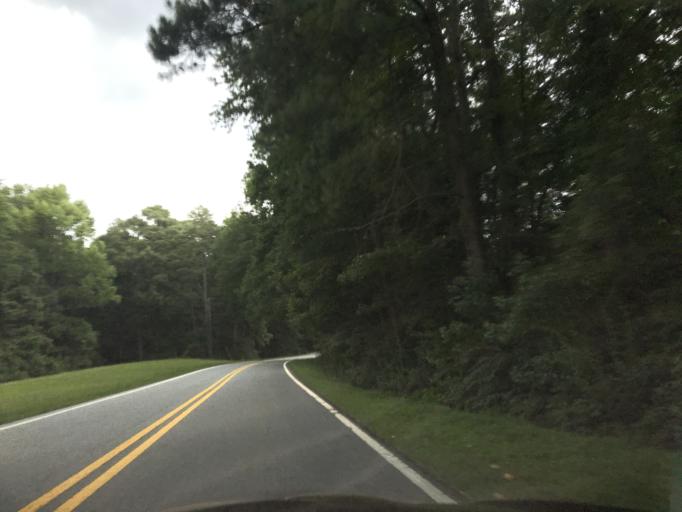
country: US
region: North Carolina
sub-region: Johnston County
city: Wilsons Mills
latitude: 35.5415
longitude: -78.4055
